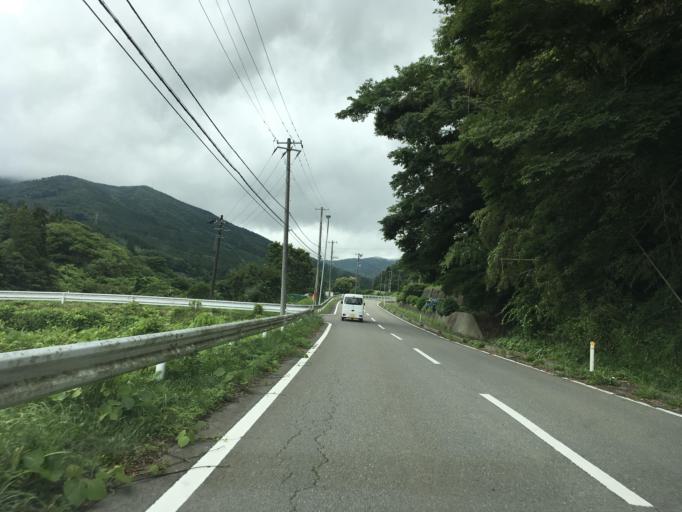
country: JP
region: Iwate
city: Ofunato
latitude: 38.8952
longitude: 141.4859
